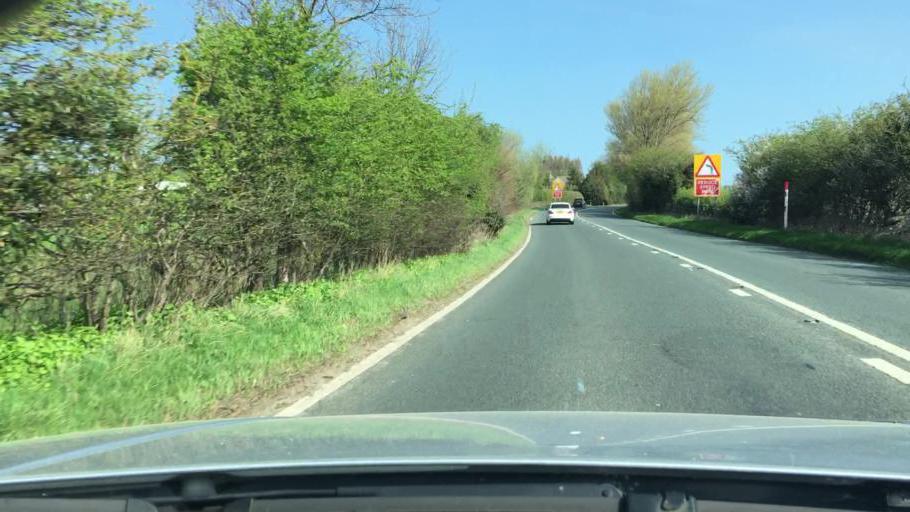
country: GB
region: England
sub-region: North Yorkshire
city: Pannal
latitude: 53.9360
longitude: -1.5368
